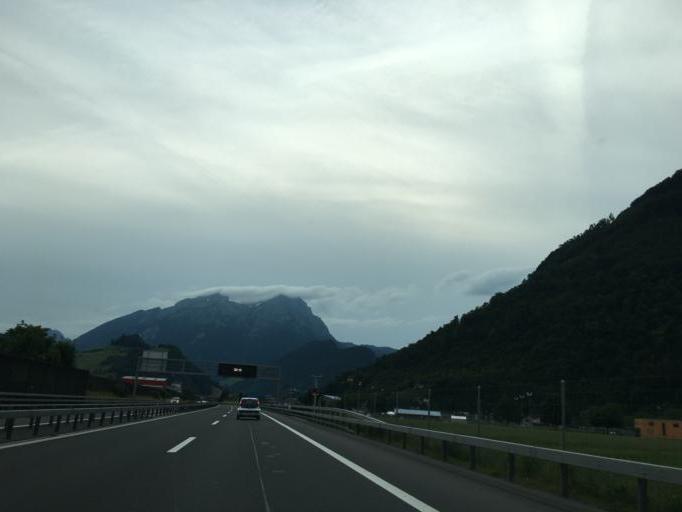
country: CH
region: Nidwalden
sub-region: Nidwalden
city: Stans
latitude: 46.9661
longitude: 8.3706
